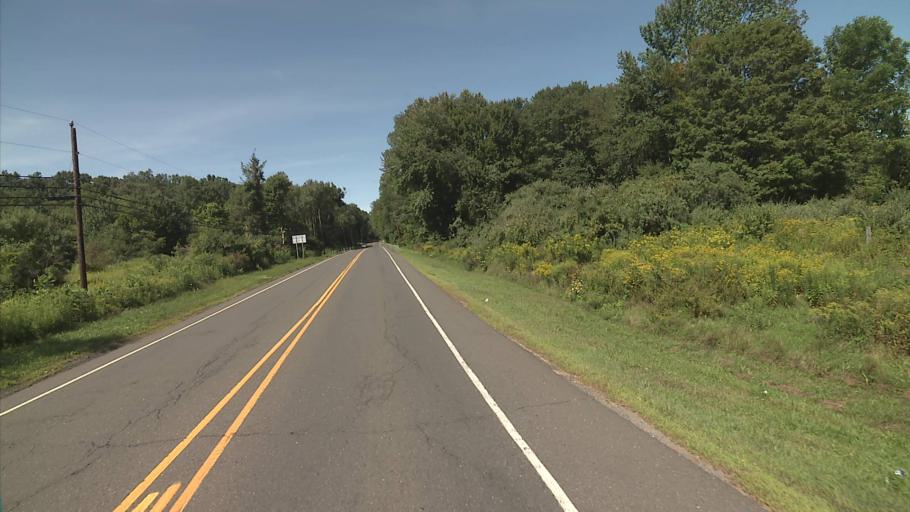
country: US
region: Connecticut
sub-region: New Haven County
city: Southbury
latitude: 41.4810
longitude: -73.1583
